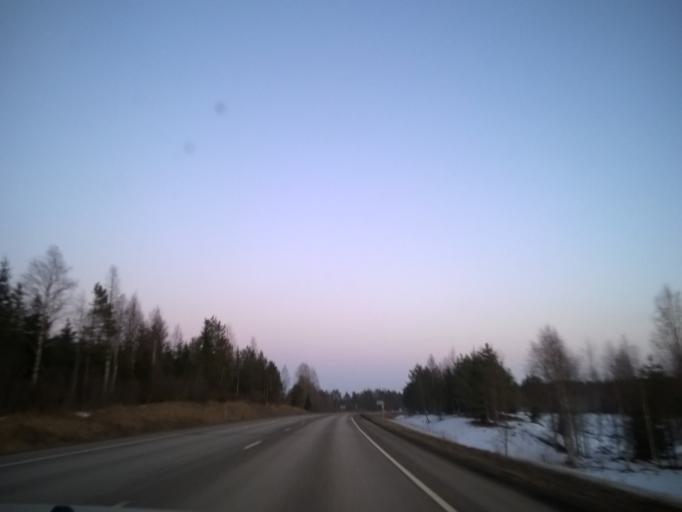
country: FI
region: Northern Ostrobothnia
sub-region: Nivala-Haapajaervi
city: Pyhaejaervi
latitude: 63.8114
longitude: 25.9067
